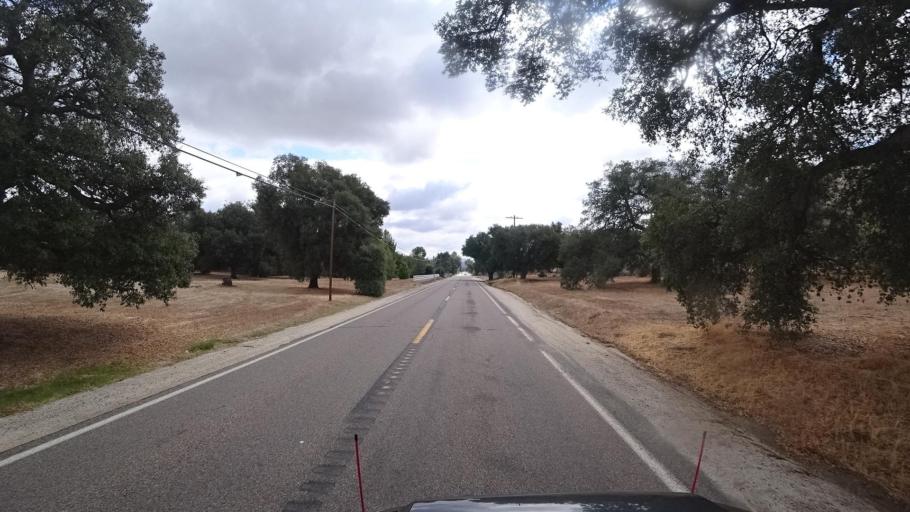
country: US
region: California
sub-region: San Diego County
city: Campo
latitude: 32.6642
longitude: -116.4881
